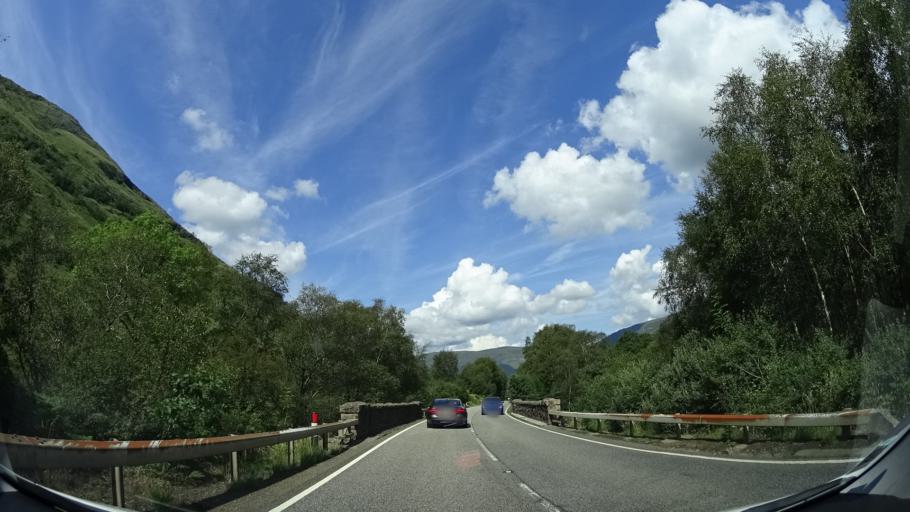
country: GB
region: Scotland
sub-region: Highland
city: Fort William
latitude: 56.6614
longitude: -5.0702
